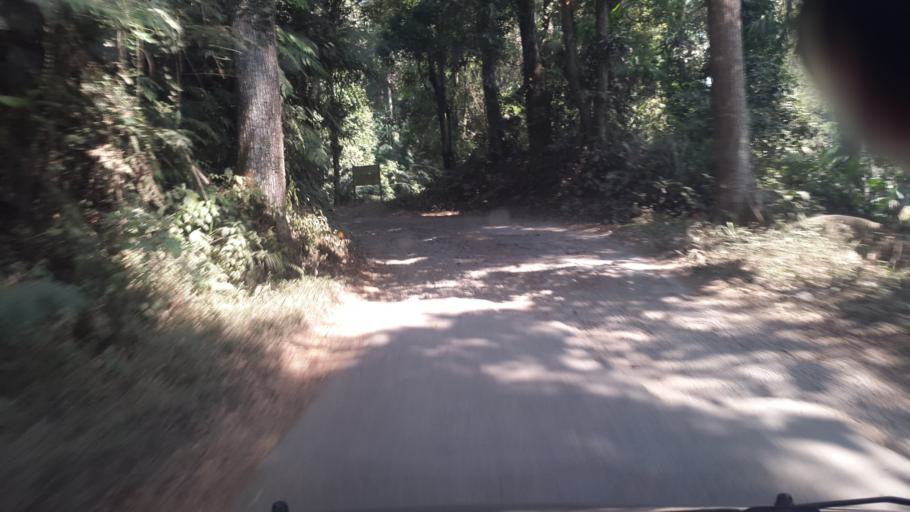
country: ID
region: West Java
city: Pasirreungit
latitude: -6.9994
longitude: 107.0066
